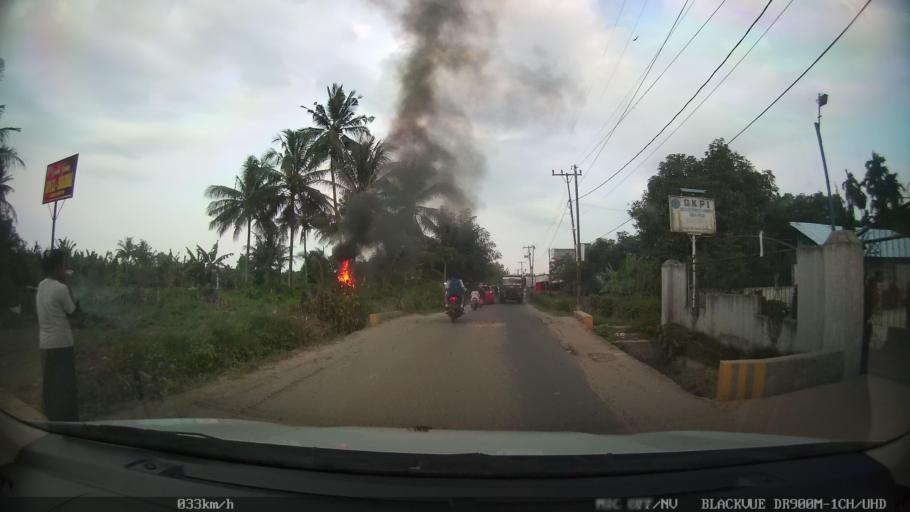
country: ID
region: North Sumatra
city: Sunggal
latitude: 3.5610
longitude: 98.5754
